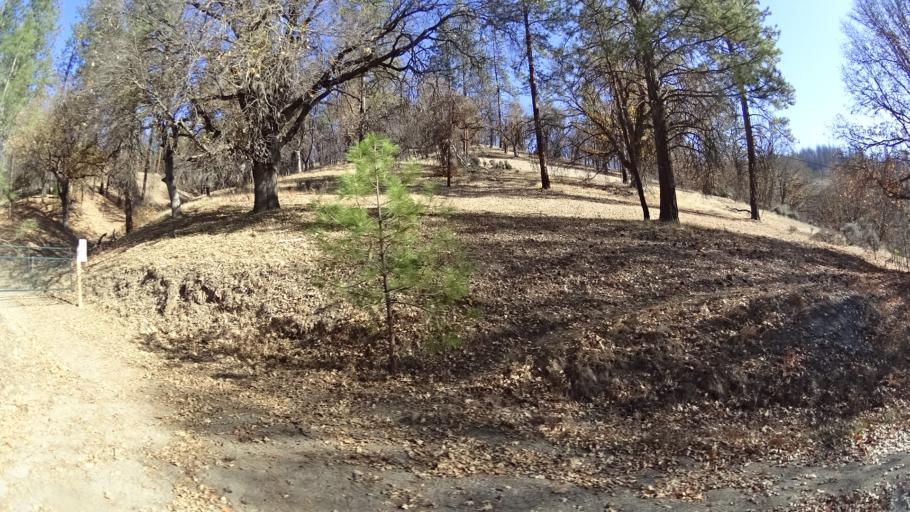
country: US
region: California
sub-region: Siskiyou County
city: Happy Camp
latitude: 41.8382
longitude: -123.0092
